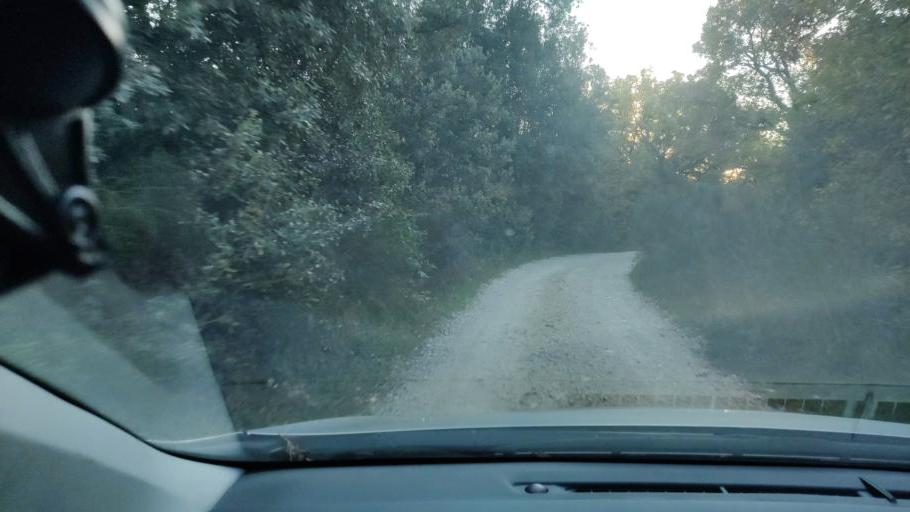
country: IT
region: Umbria
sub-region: Provincia di Terni
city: Amelia
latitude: 42.5823
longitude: 12.4320
